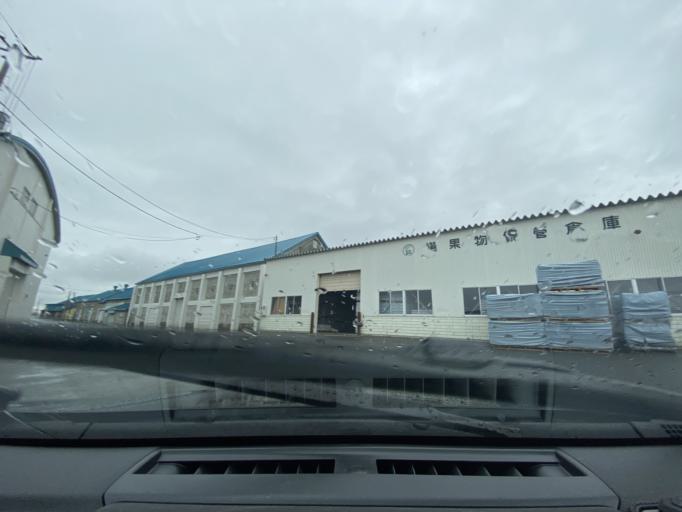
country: JP
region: Hokkaido
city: Fukagawa
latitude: 43.8105
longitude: 141.9321
